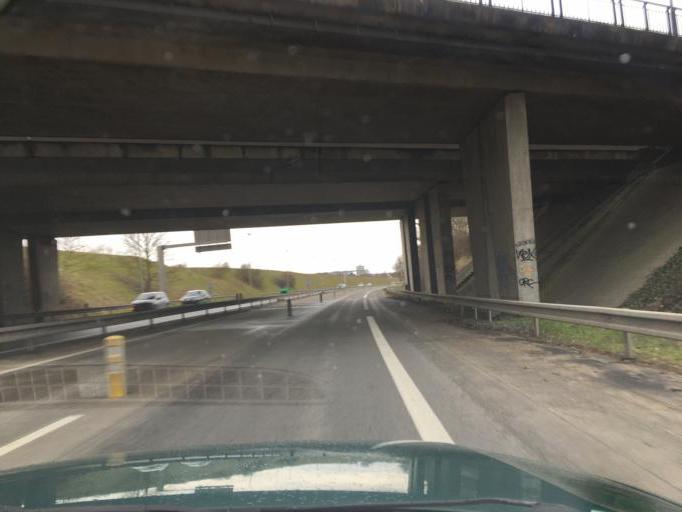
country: FR
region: Centre
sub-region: Departement du Loiret
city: Saran
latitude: 47.9404
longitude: 1.8889
